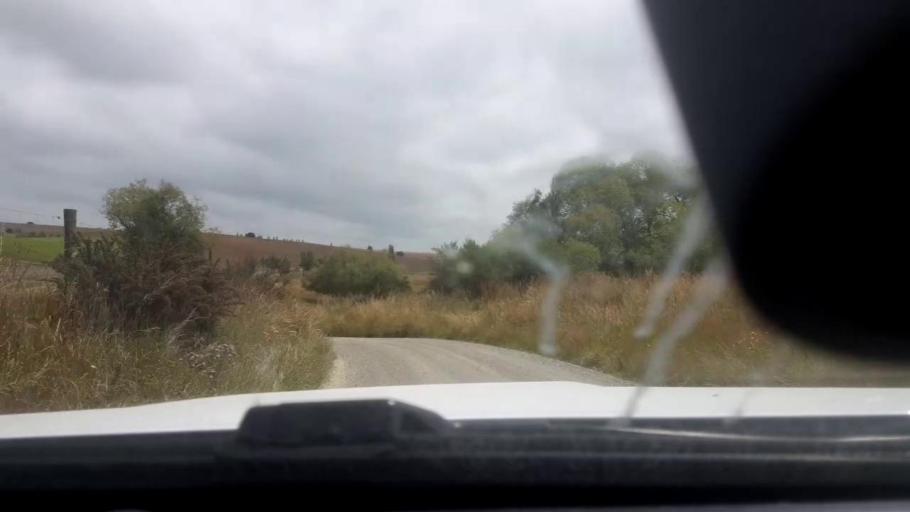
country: NZ
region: Canterbury
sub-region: Timaru District
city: Pleasant Point
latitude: -44.2030
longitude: 171.1958
